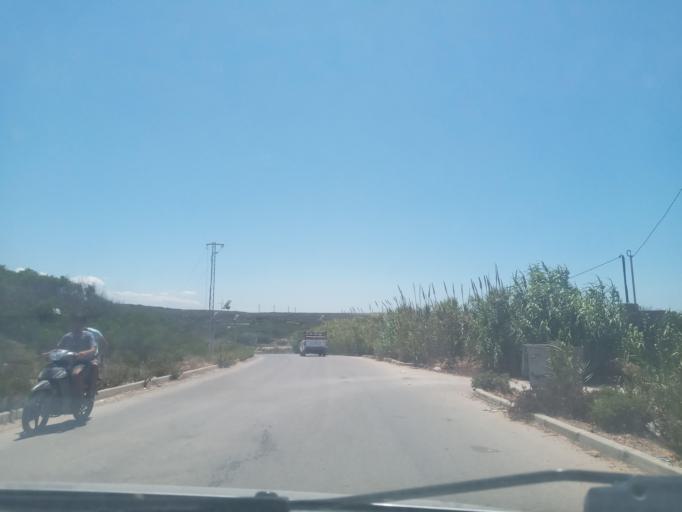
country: TN
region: Nabul
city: El Haouaria
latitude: 37.0501
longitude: 10.9812
